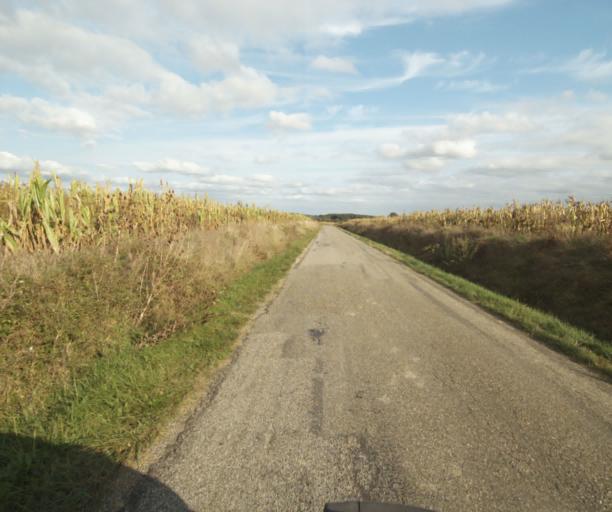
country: FR
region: Midi-Pyrenees
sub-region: Departement du Tarn-et-Garonne
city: Verdun-sur-Garonne
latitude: 43.8384
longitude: 1.1378
